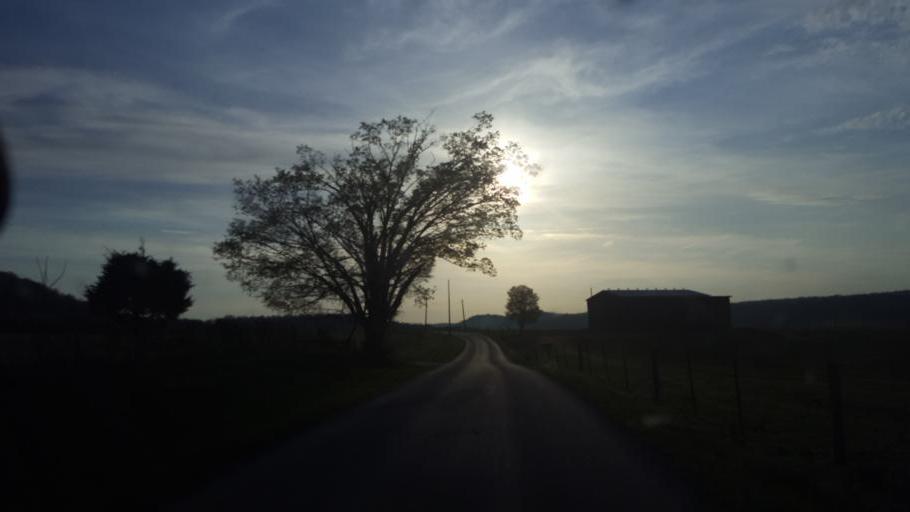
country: US
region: Kentucky
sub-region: Hart County
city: Horse Cave
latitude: 37.2236
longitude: -85.9465
